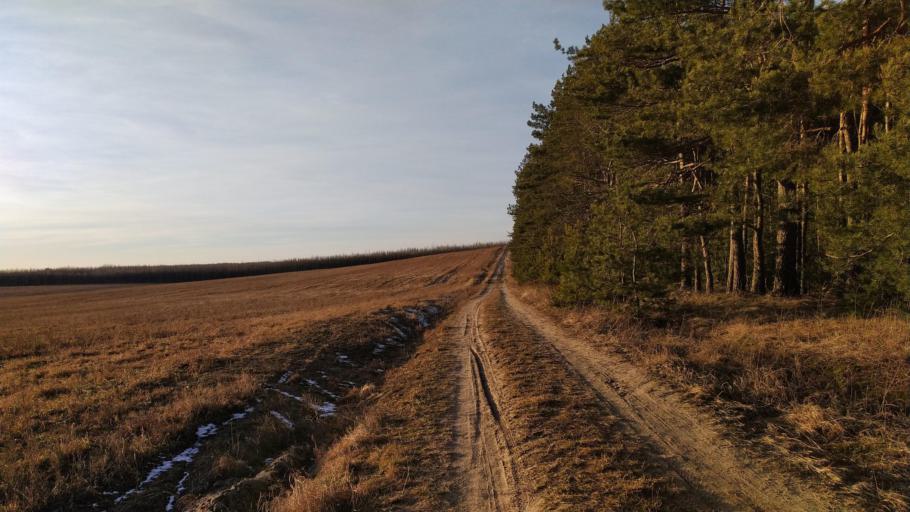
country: BY
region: Brest
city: Kamyanyets
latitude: 52.3795
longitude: 23.8403
